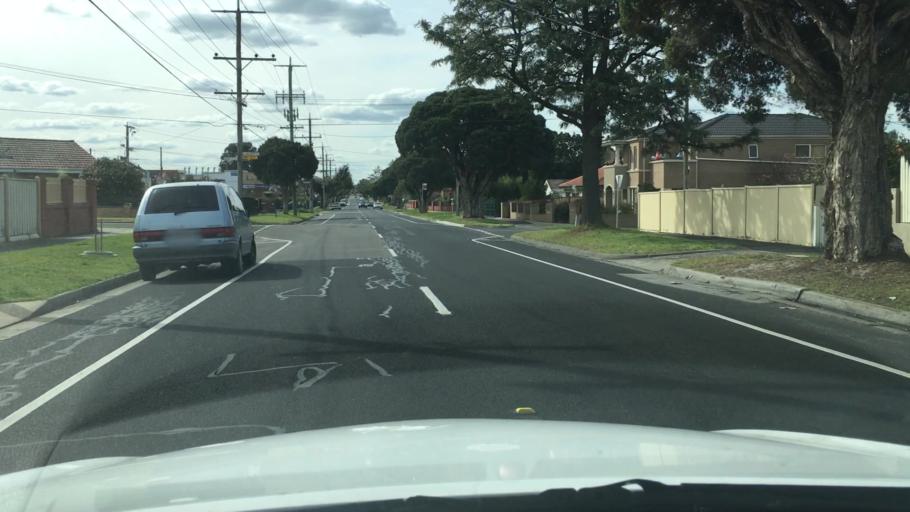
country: AU
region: Victoria
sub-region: Greater Dandenong
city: Springvale South
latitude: -37.9601
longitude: 145.1570
